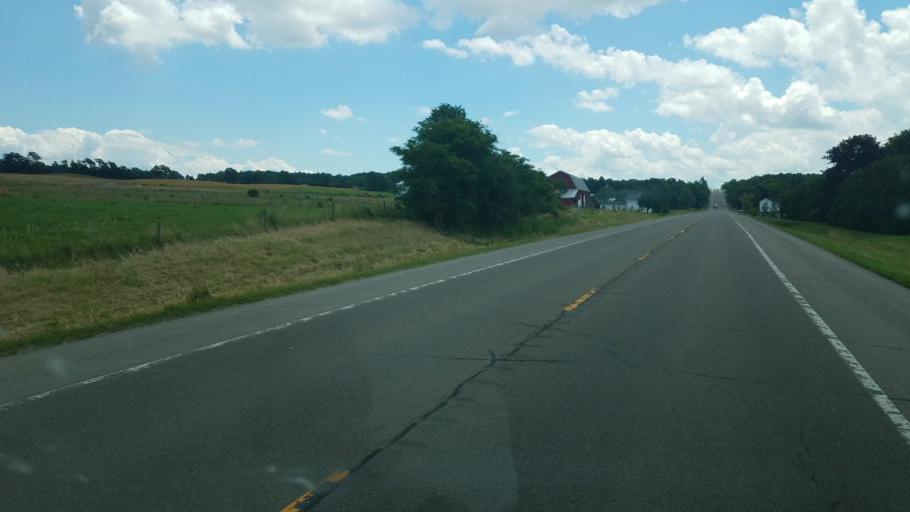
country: US
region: New York
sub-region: Yates County
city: Keuka Park
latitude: 42.6005
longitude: -77.0376
